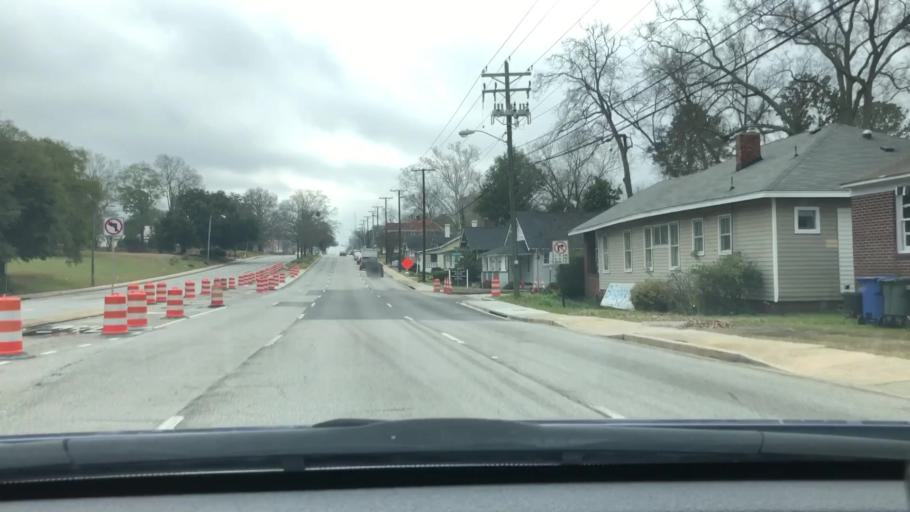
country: US
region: South Carolina
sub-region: Richland County
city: Columbia
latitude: 34.0186
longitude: -81.0359
